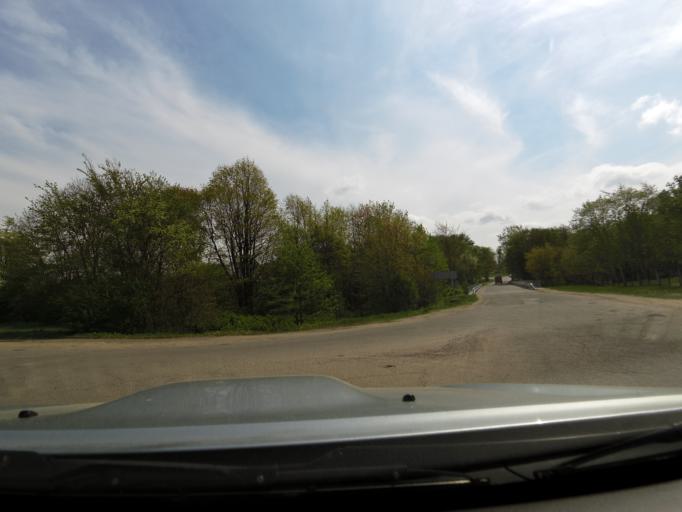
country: LT
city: Salcininkai
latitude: 54.4354
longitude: 25.3000
